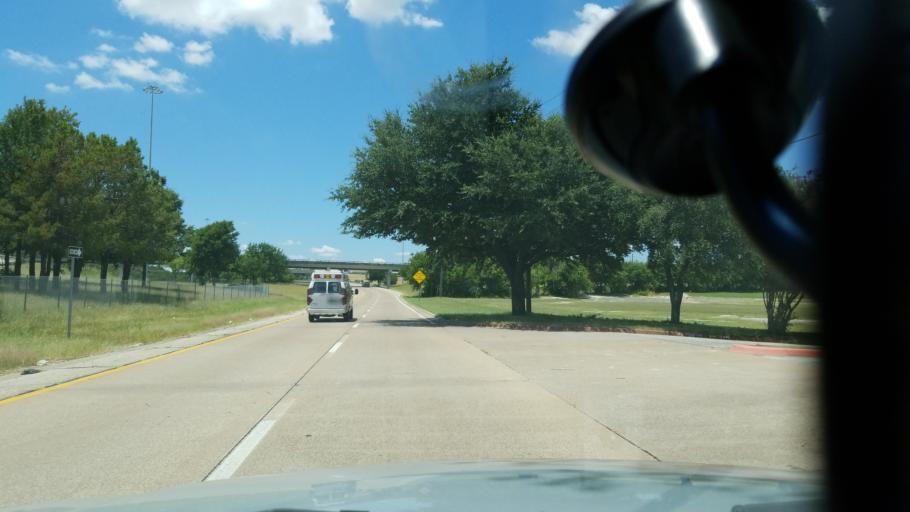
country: US
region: Texas
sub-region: Dallas County
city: Duncanville
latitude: 32.6567
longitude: -96.8766
